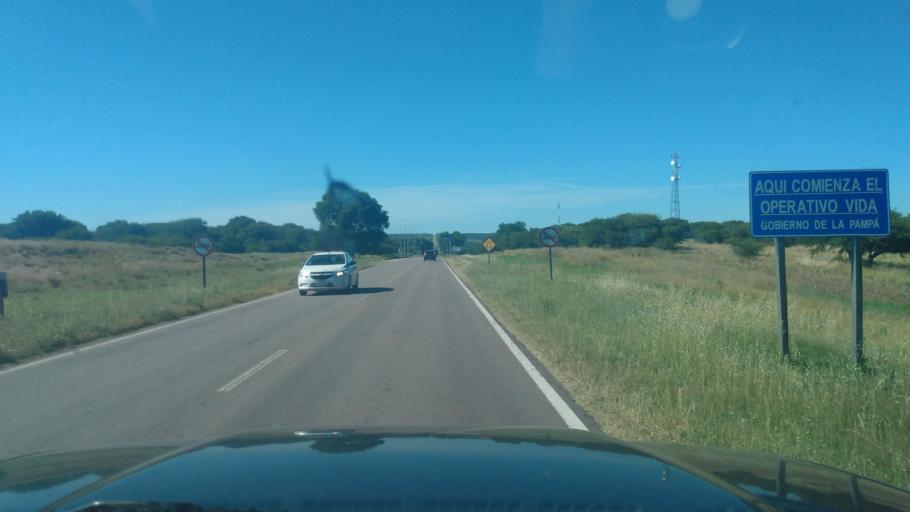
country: AR
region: La Pampa
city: Doblas
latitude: -37.3021
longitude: -64.2879
